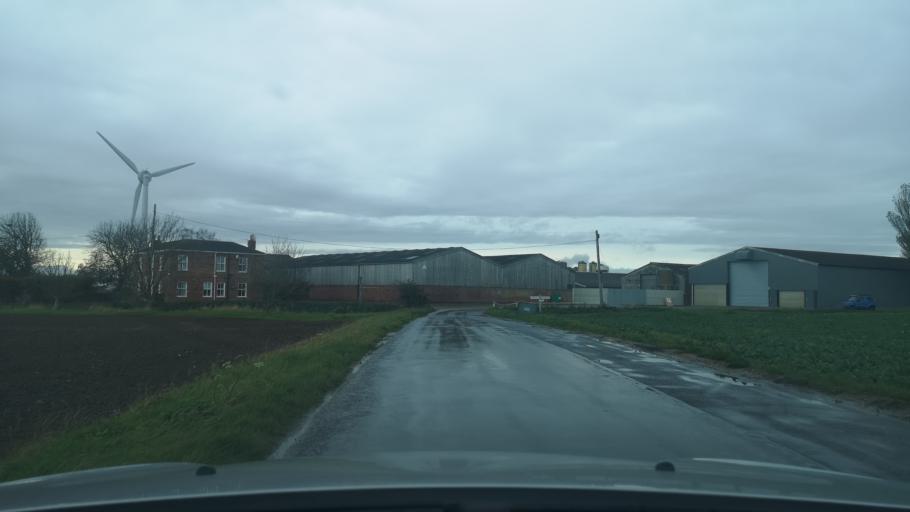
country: GB
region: England
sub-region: East Riding of Yorkshire
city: Easington
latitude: 53.6668
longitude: 0.0888
